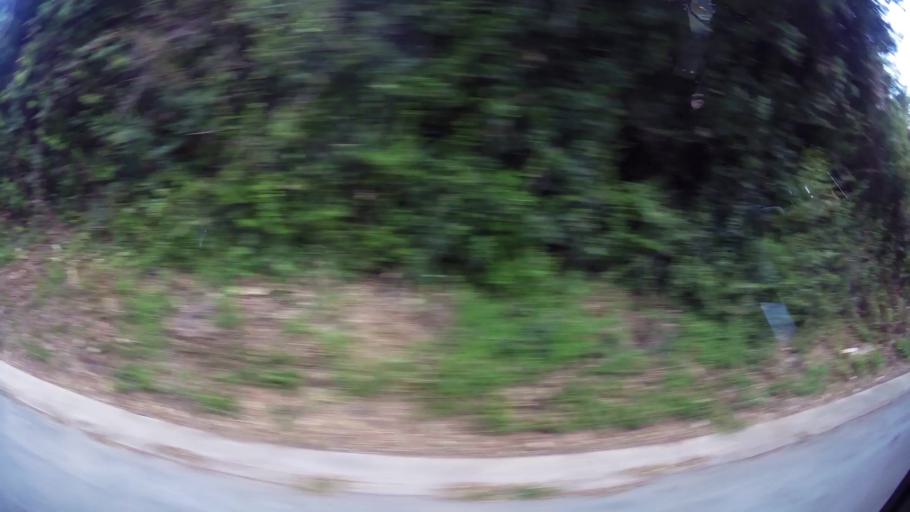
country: ZA
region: Western Cape
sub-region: Eden District Municipality
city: Plettenberg Bay
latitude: -34.0484
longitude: 23.3700
